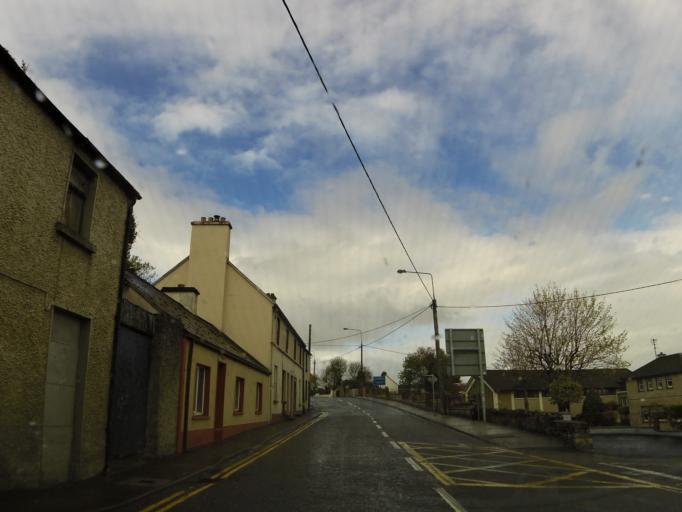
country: IE
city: Ballisodare
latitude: 54.2095
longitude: -8.5108
